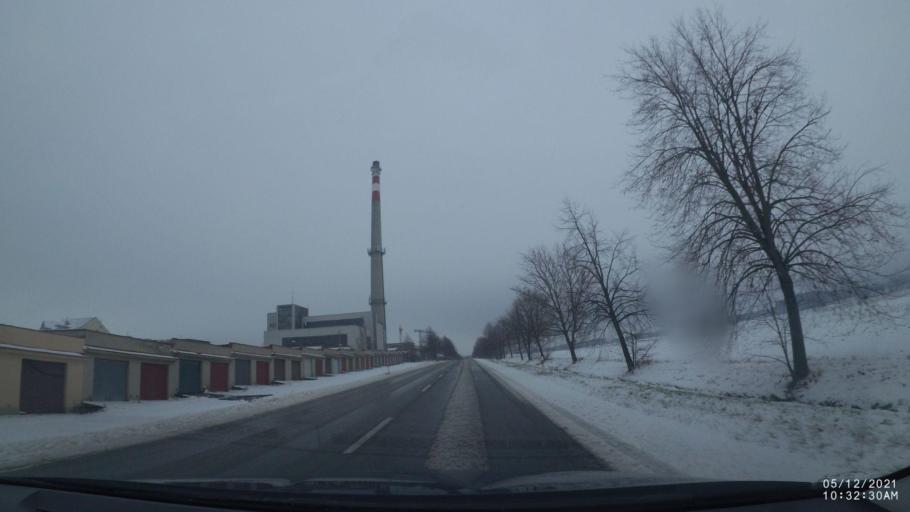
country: CZ
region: Kralovehradecky
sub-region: Okres Rychnov nad Kneznou
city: Rychnov nad Kneznou
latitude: 50.1595
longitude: 16.2871
